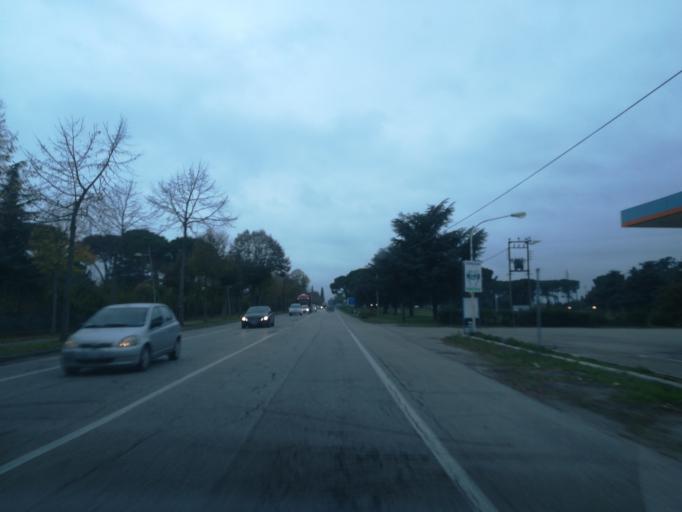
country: IT
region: Emilia-Romagna
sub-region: Provincia di Bologna
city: Imola
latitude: 44.3681
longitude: 11.6767
